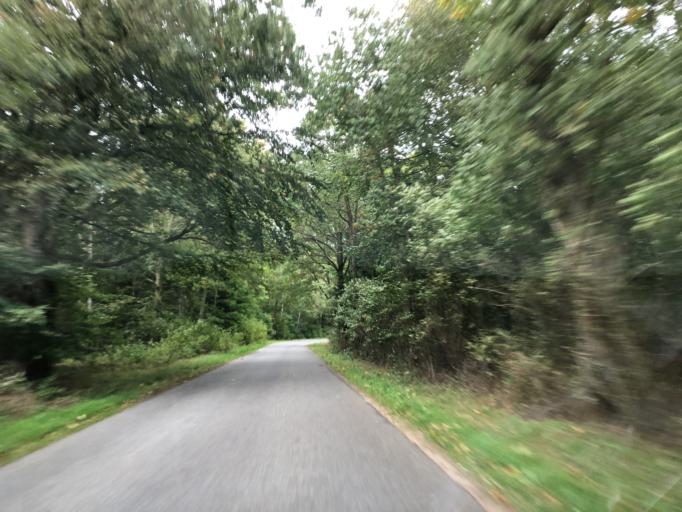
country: DK
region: Central Jutland
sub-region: Viborg Kommune
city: Viborg
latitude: 56.4212
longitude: 9.3242
